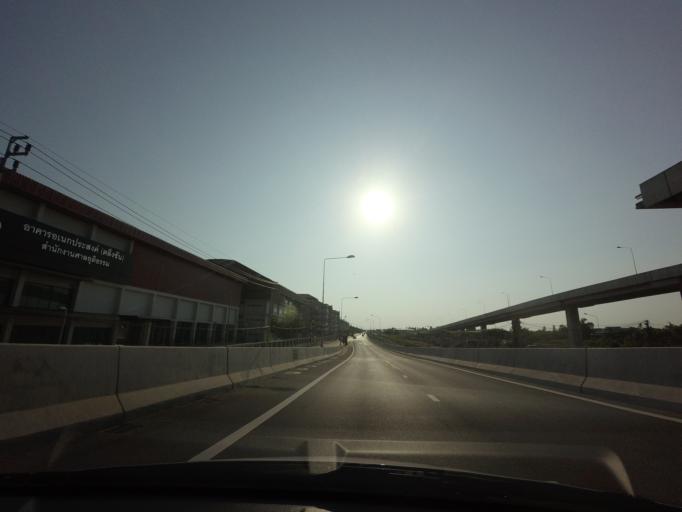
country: TH
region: Bangkok
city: Taling Chan
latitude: 13.7989
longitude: 100.4239
